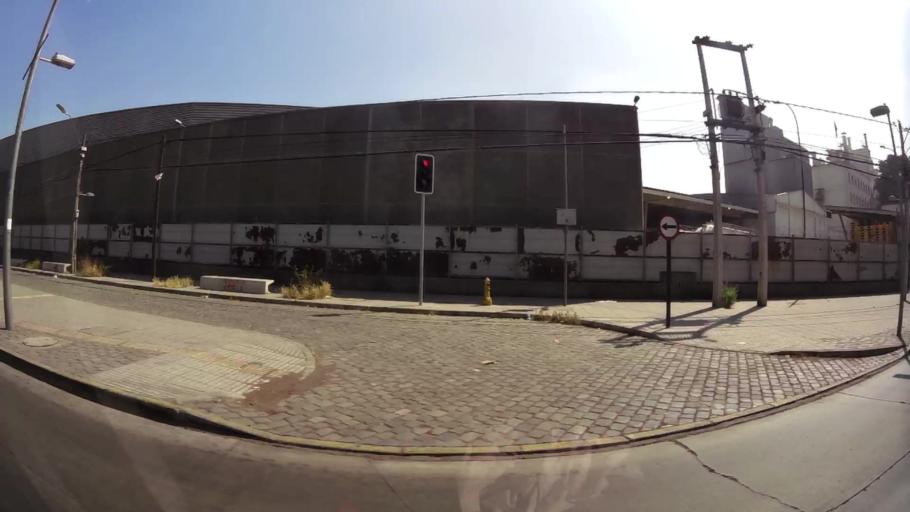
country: CL
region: Santiago Metropolitan
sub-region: Provincia de Santiago
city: Santiago
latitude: -33.4697
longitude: -70.6794
